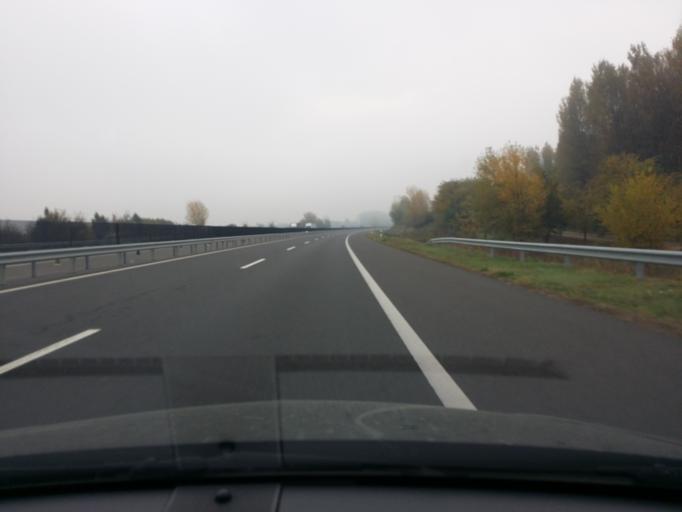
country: HU
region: Szabolcs-Szatmar-Bereg
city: Kalmanhaza
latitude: 47.9027
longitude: 21.5883
